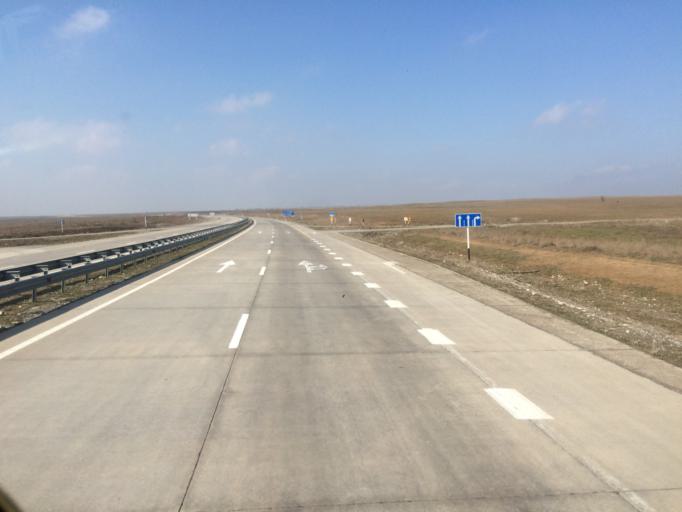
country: KZ
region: Ongtustik Qazaqstan
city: Shymkent
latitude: 42.4878
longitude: 69.5194
